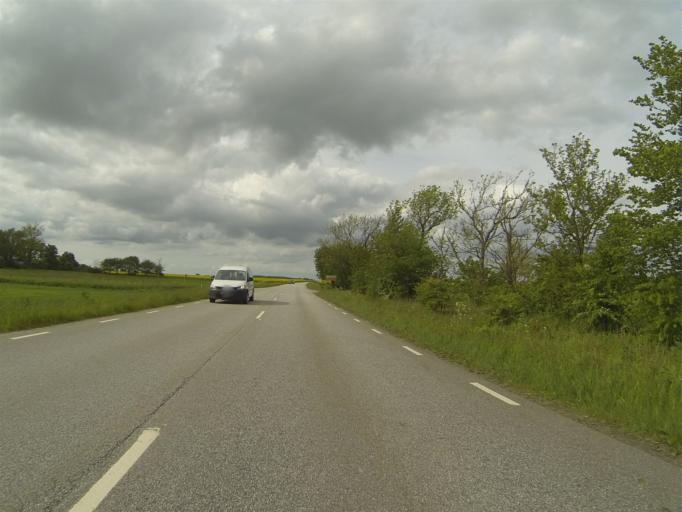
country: SE
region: Skane
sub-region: Lunds Kommun
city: Lund
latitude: 55.6988
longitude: 13.3059
